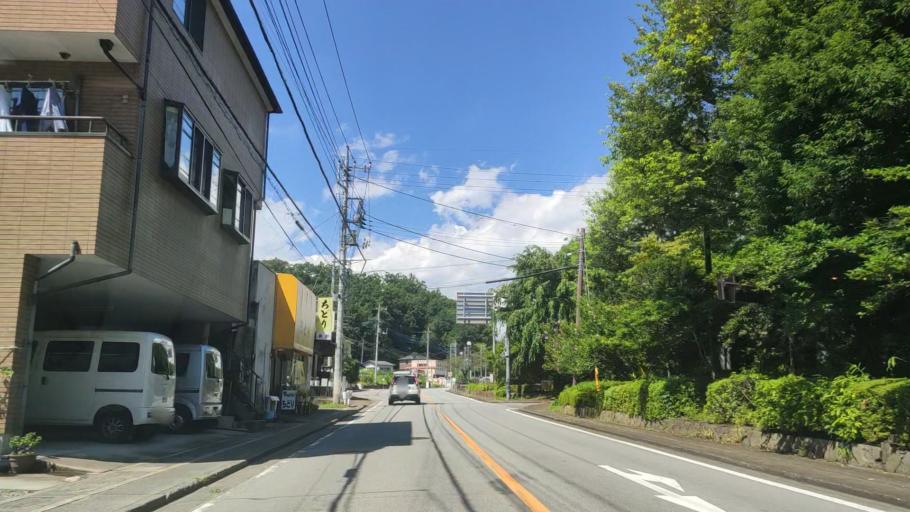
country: JP
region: Yamanashi
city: Enzan
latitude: 35.6931
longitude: 138.6808
